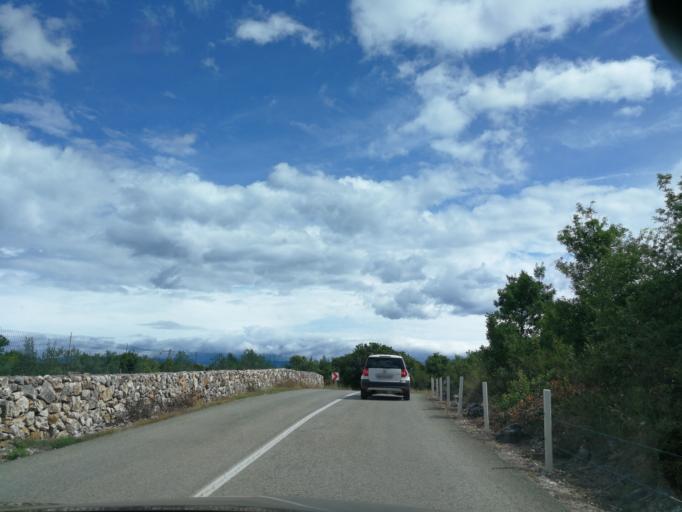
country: HR
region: Primorsko-Goranska
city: Punat
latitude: 45.0783
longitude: 14.6578
